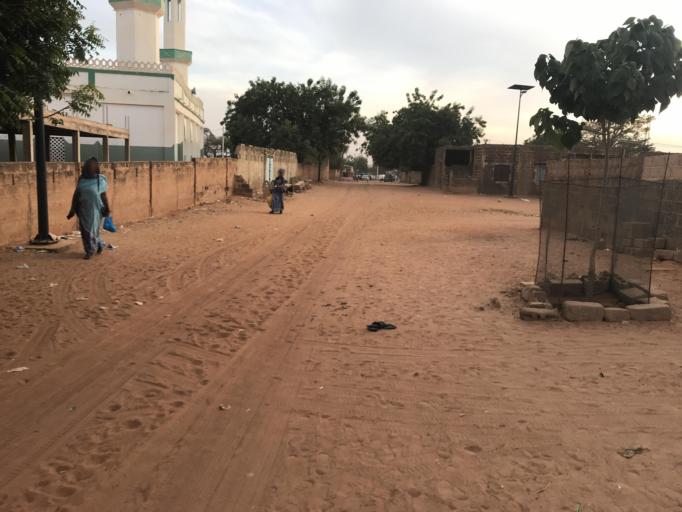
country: SN
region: Louga
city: Ndibene Dahra
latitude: 15.3940
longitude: -15.1131
